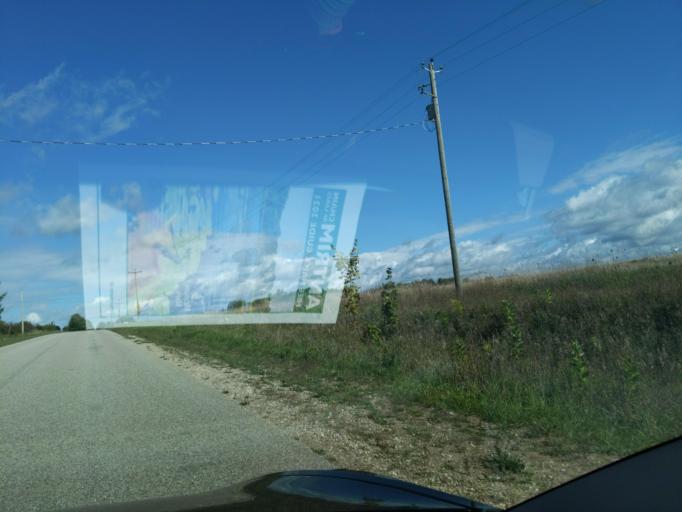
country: US
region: Michigan
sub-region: Antrim County
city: Elk Rapids
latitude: 44.9501
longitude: -85.3324
